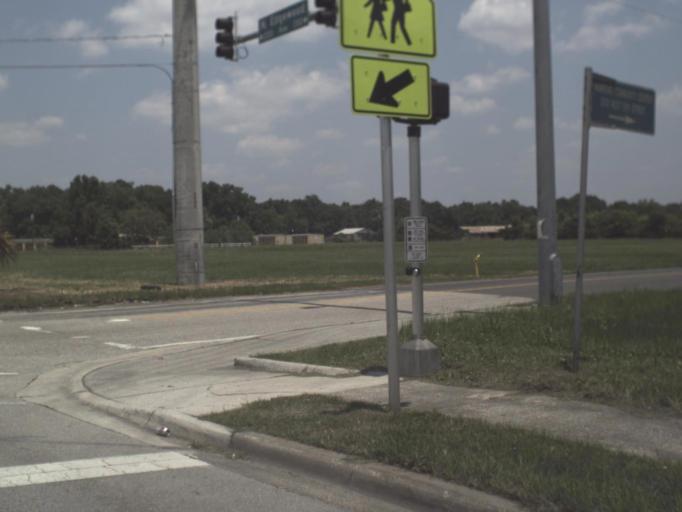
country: US
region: Florida
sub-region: Duval County
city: Jacksonville
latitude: 30.3509
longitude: -81.7311
